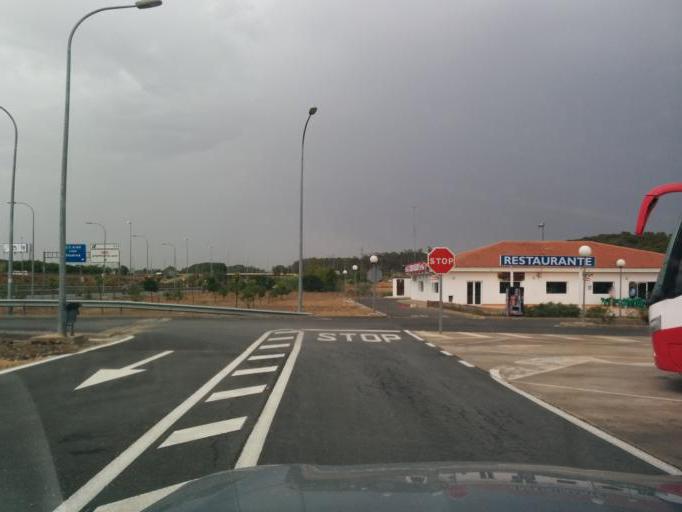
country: ES
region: Andalusia
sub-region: Provincia de Huelva
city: Ayamonte
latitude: 37.2384
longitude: -7.3844
